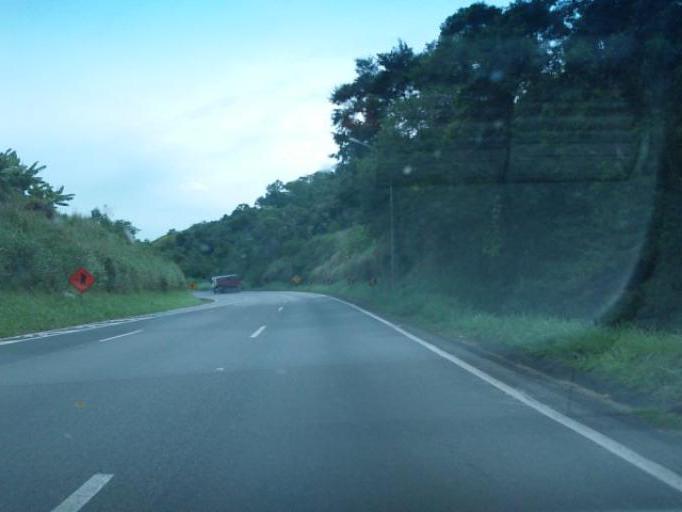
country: BR
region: Sao Paulo
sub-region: Cajati
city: Cajati
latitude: -24.8183
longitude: -48.2145
